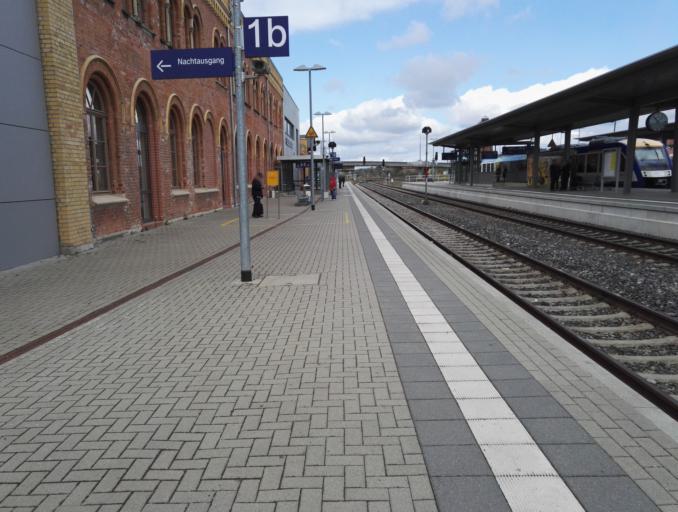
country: DE
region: Saxony-Anhalt
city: Halberstadt
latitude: 51.8992
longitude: 11.0738
